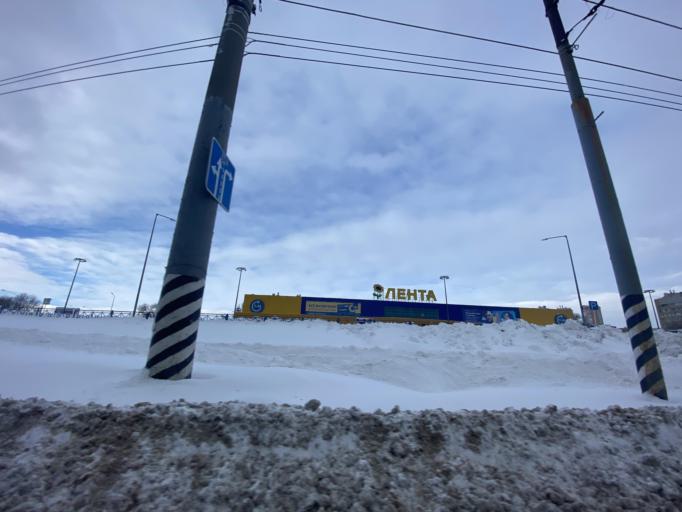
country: RU
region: Saratov
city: Engel's
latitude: 51.4963
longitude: 46.0931
